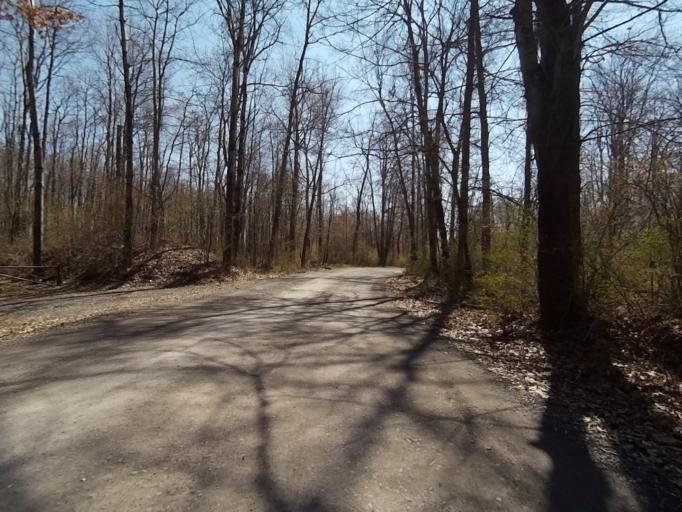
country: US
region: Pennsylvania
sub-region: Centre County
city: Park Forest Village
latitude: 40.7984
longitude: -77.9465
